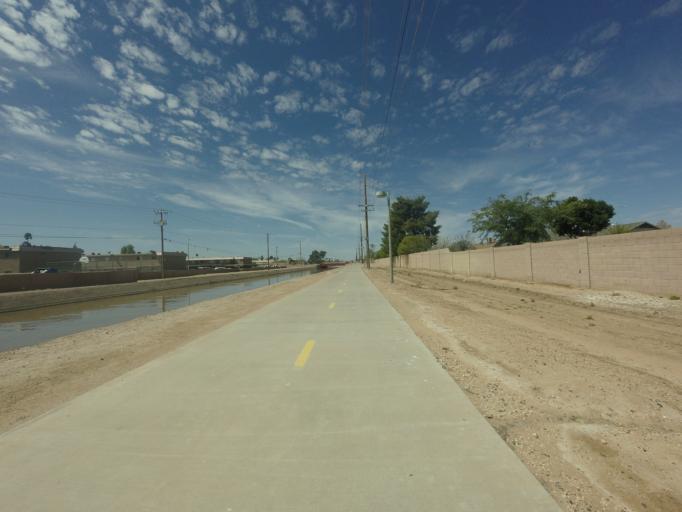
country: US
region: Arizona
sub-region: Maricopa County
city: Mesa
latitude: 33.4370
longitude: -111.8124
